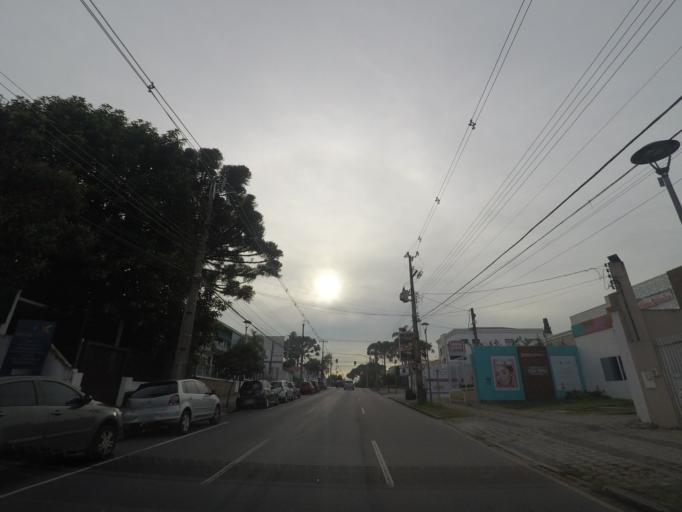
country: BR
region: Parana
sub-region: Curitiba
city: Curitiba
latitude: -25.4403
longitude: -49.2948
